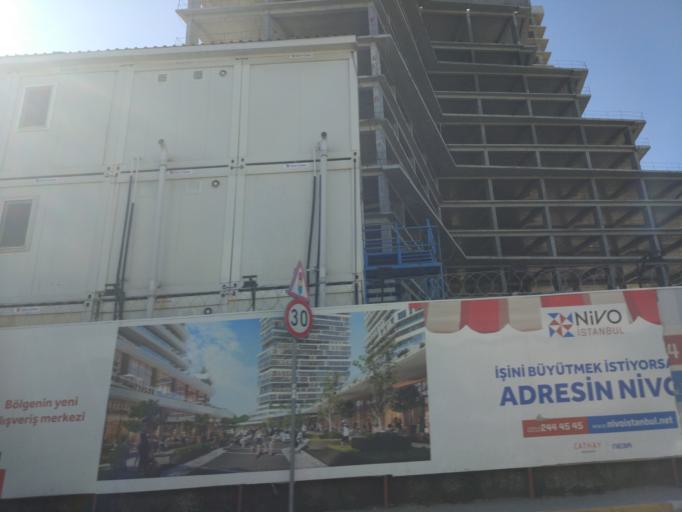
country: TR
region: Istanbul
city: Mahmutbey
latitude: 41.0274
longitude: 28.8076
